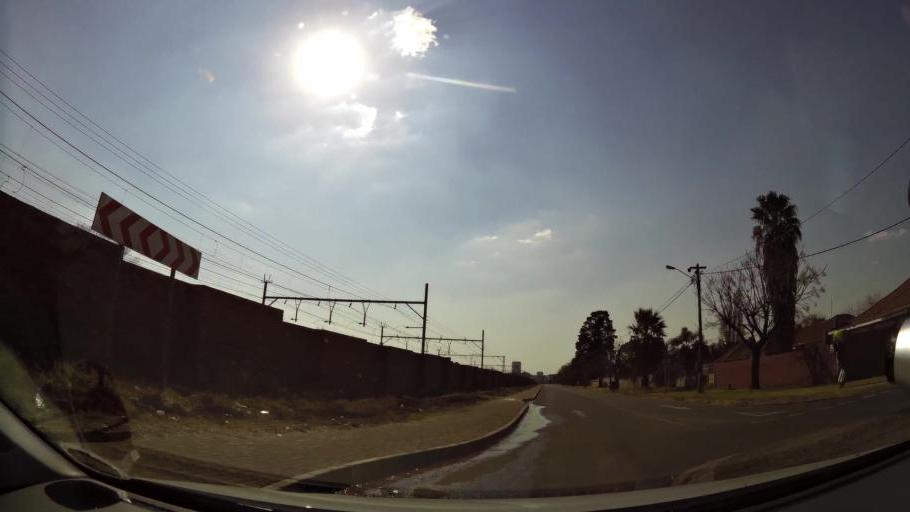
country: ZA
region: Gauteng
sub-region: City of Johannesburg Metropolitan Municipality
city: Modderfontein
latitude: -26.1221
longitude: 28.2265
